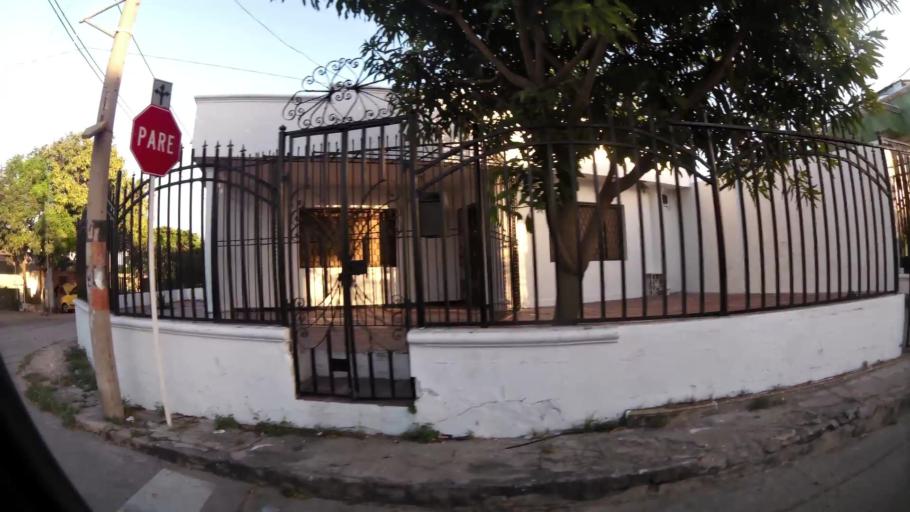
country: CO
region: Atlantico
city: Barranquilla
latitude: 10.9782
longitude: -74.7953
